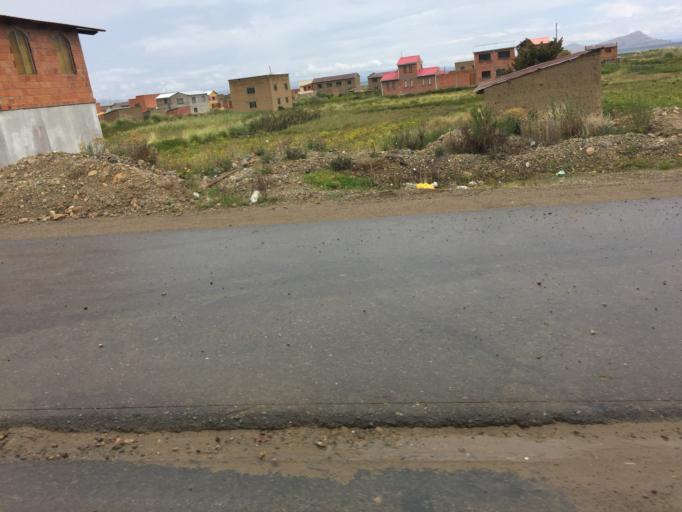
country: BO
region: La Paz
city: Huatajata
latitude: -16.2056
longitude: -68.7053
